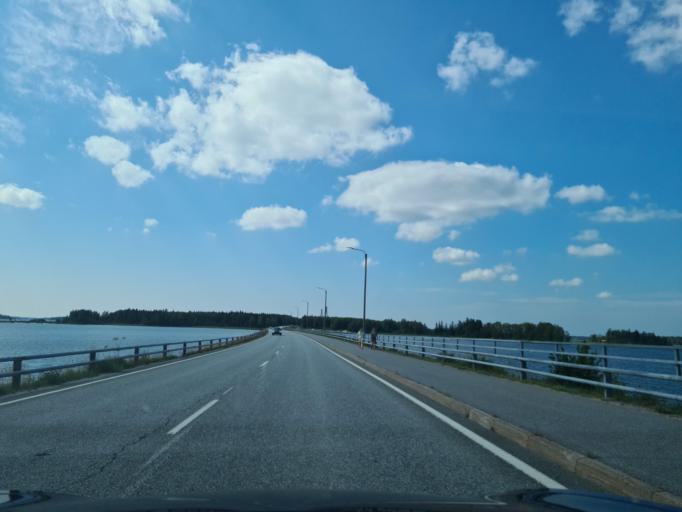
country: FI
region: Ostrobothnia
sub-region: Vaasa
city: Replot
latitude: 63.2056
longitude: 21.5130
